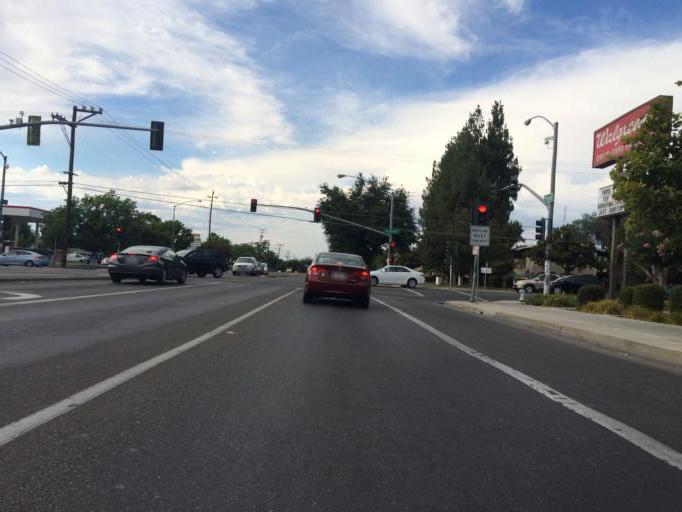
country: US
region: California
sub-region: Fresno County
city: Fresno
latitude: 36.7937
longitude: -119.7723
